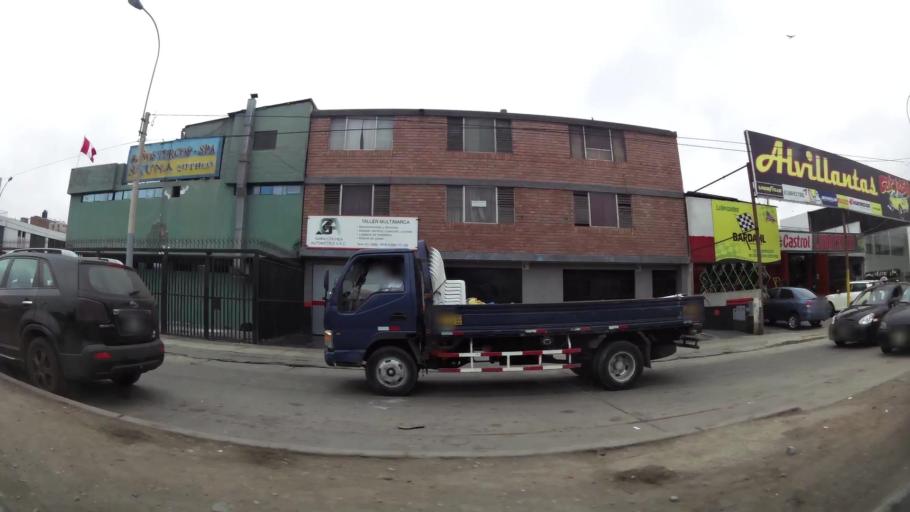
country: PE
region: Callao
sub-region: Callao
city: Callao
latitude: -12.0731
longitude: -77.1018
